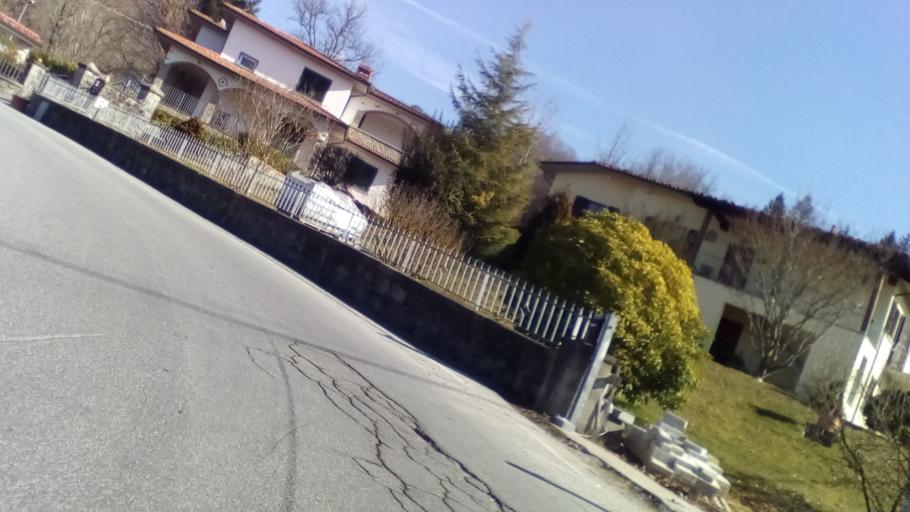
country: IT
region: Tuscany
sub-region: Provincia di Lucca
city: Pieve Fosciana
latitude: 44.1389
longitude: 10.4207
